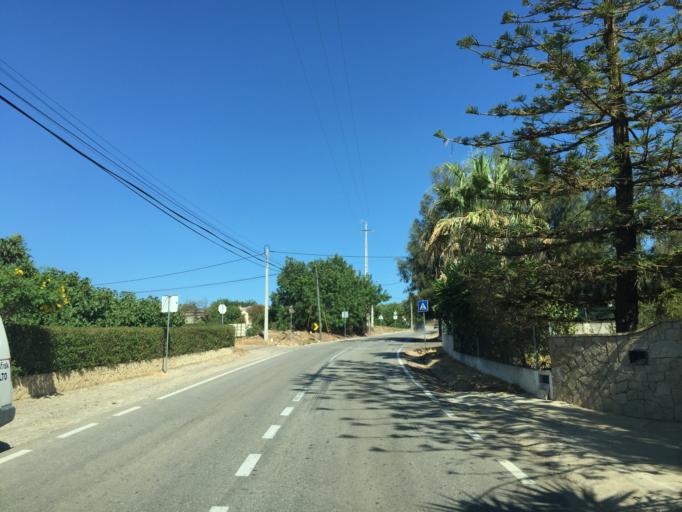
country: PT
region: Faro
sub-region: Loule
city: Vilamoura
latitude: 37.1138
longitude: -8.0909
